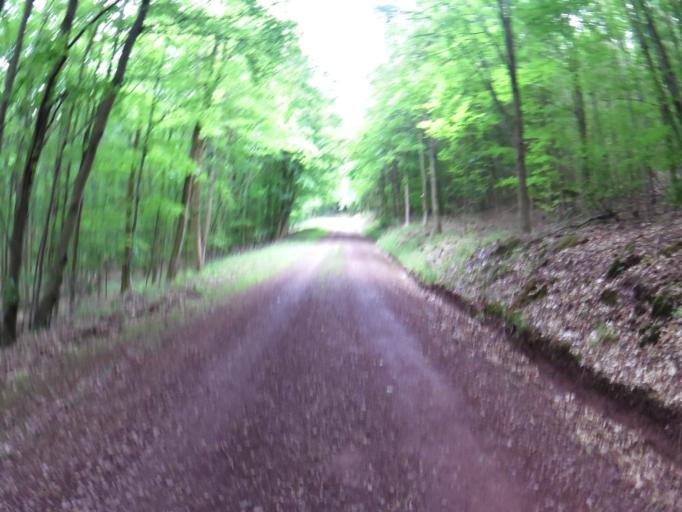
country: DE
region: Thuringia
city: Eisenach
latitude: 50.9499
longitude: 10.3130
